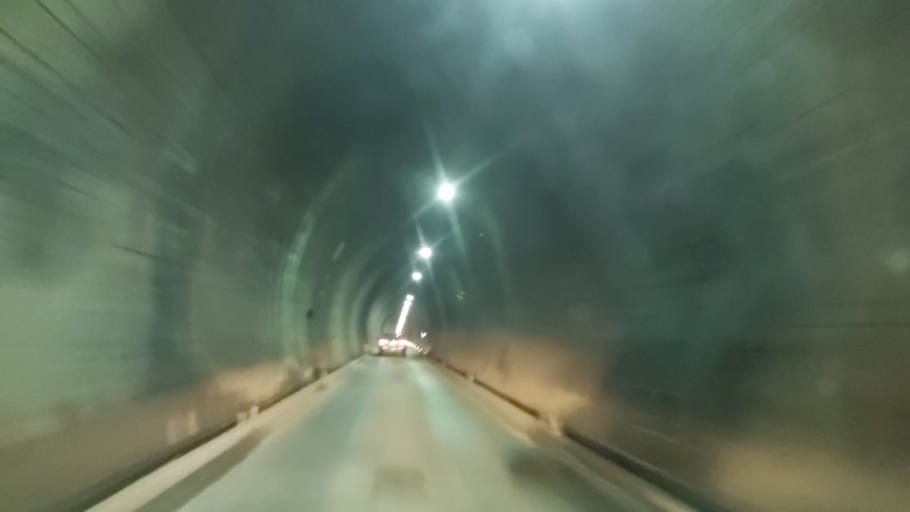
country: CL
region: Araucania
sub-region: Provincia de Cautin
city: Vilcun
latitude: -38.5292
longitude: -71.5113
